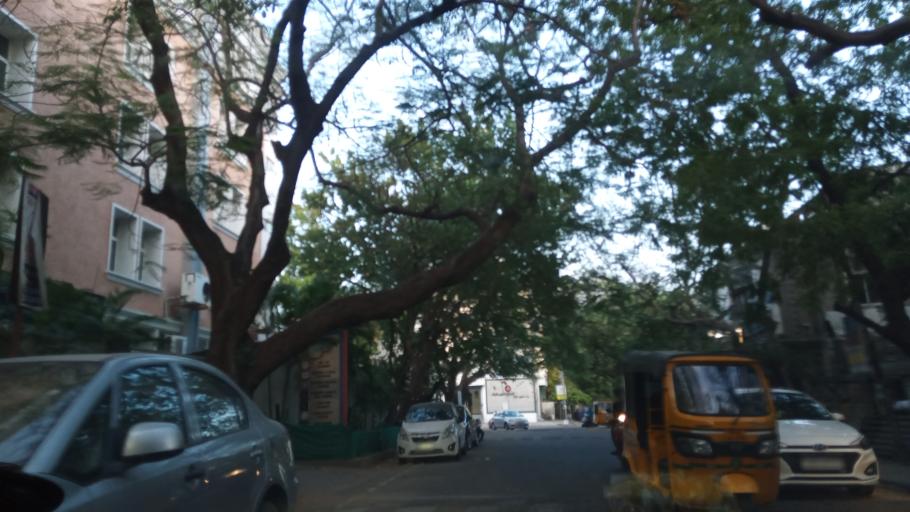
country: IN
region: Tamil Nadu
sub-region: Kancheepuram
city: Alandur
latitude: 13.0390
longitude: 80.2160
